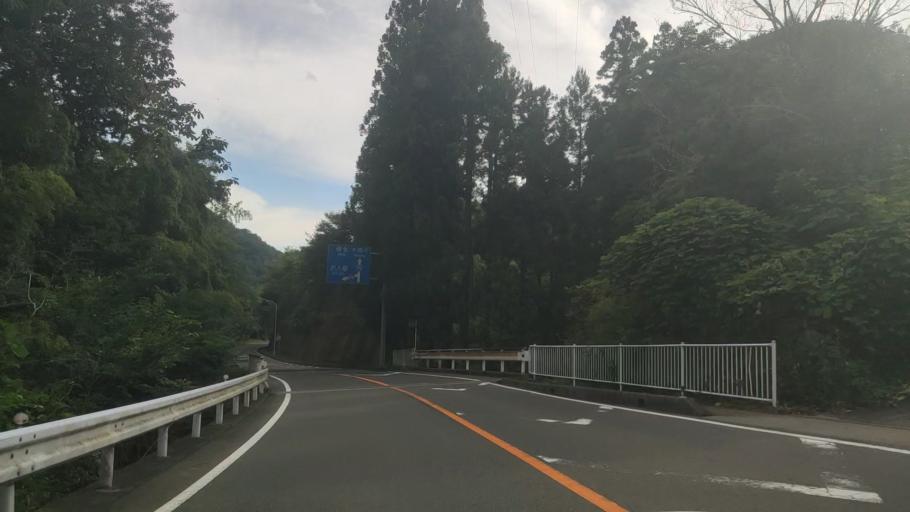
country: JP
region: Gunma
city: Omamacho-omama
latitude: 36.5797
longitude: 139.3900
